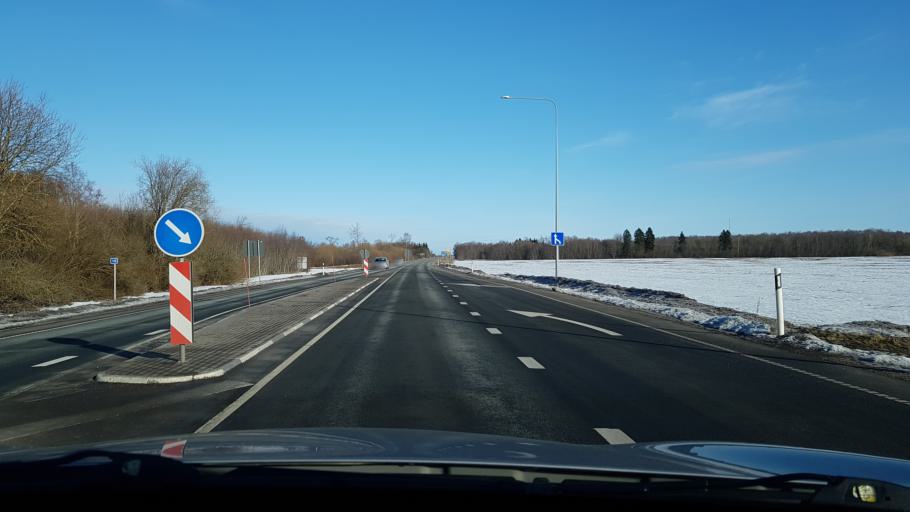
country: EE
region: Viljandimaa
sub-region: Vohma linn
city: Vohma
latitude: 58.6321
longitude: 25.5721
